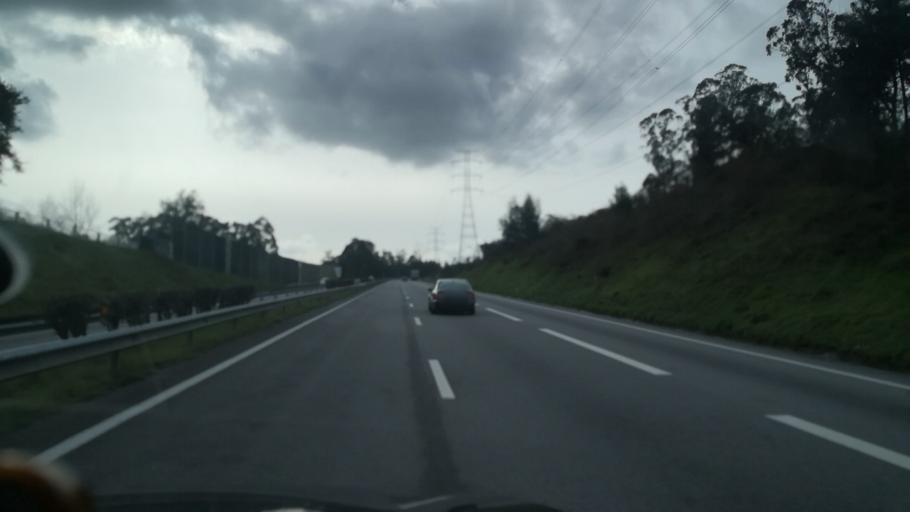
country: PT
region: Porto
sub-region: Paredes
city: Baltar
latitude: 41.1921
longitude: -8.3592
